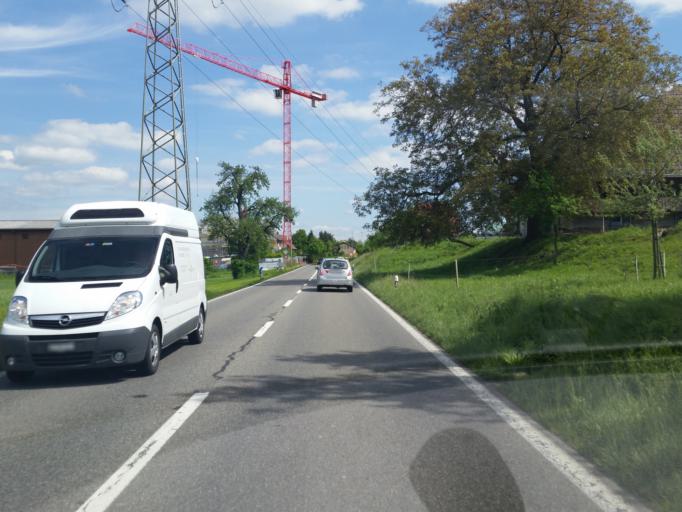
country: CH
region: Aargau
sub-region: Bezirk Bremgarten
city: Wohlen
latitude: 47.3412
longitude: 8.2715
